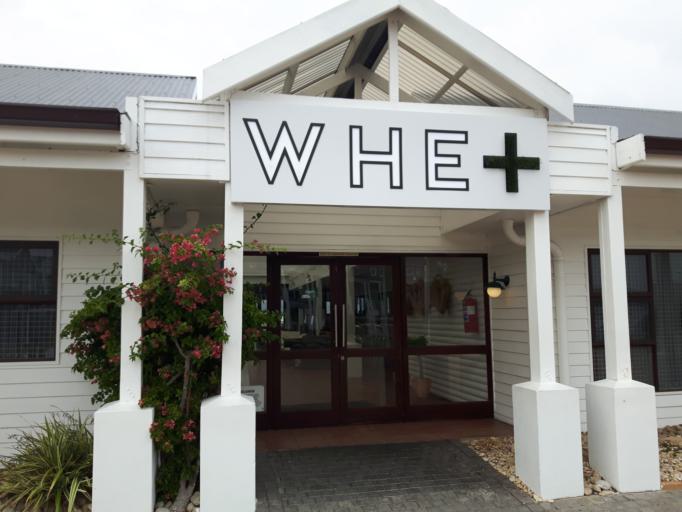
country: ZA
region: Western Cape
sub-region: Eden District Municipality
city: Knysna
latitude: -34.0488
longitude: 23.0470
